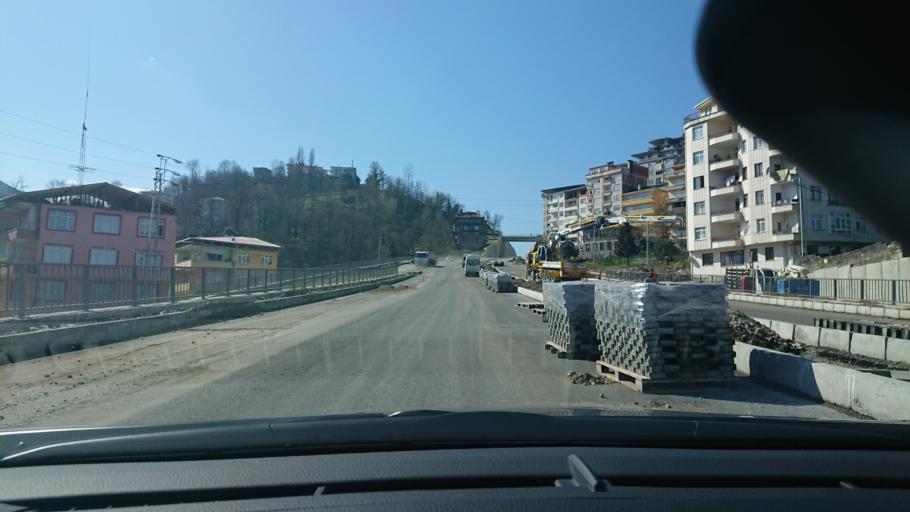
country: TR
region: Rize
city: Rize
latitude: 41.0202
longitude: 40.5239
